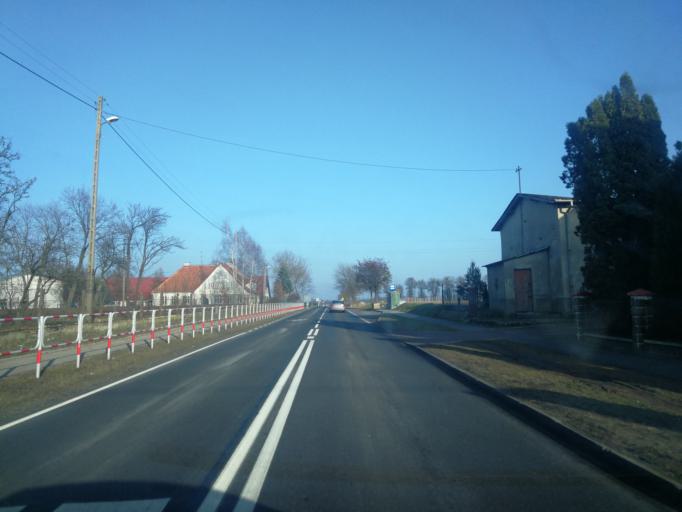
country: PL
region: Warmian-Masurian Voivodeship
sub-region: Powiat ilawski
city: Lubawa
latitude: 53.5852
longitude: 19.8345
